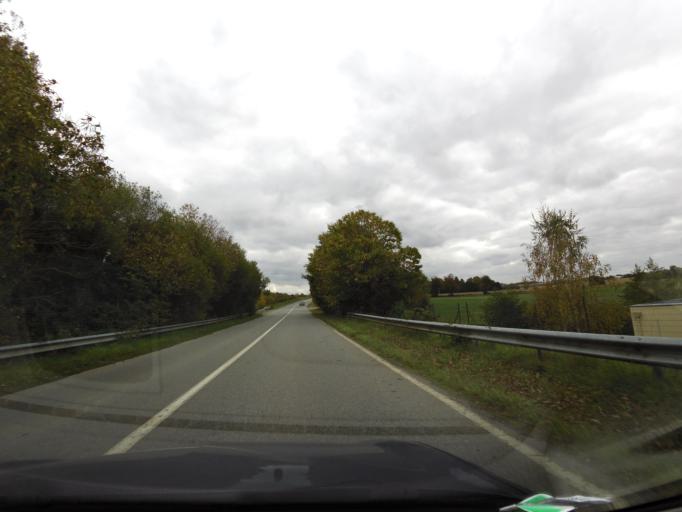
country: FR
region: Brittany
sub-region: Departement d'Ille-et-Vilaine
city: Saint-Armel
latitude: 47.9980
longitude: -1.5936
